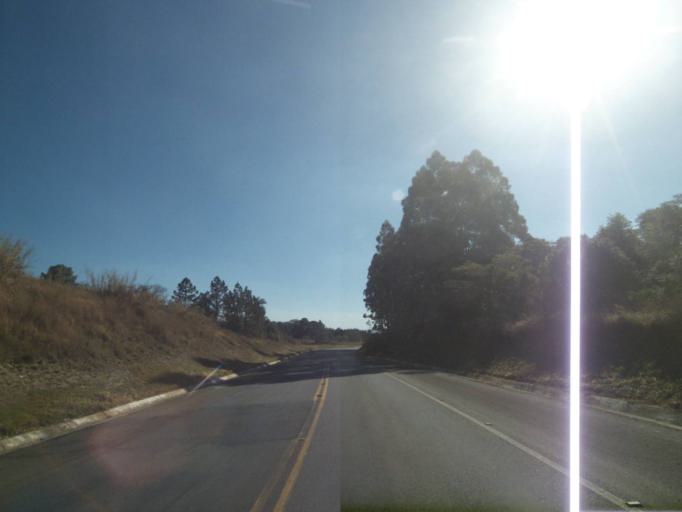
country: BR
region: Parana
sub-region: Tibagi
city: Tibagi
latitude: -24.7897
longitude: -50.4683
